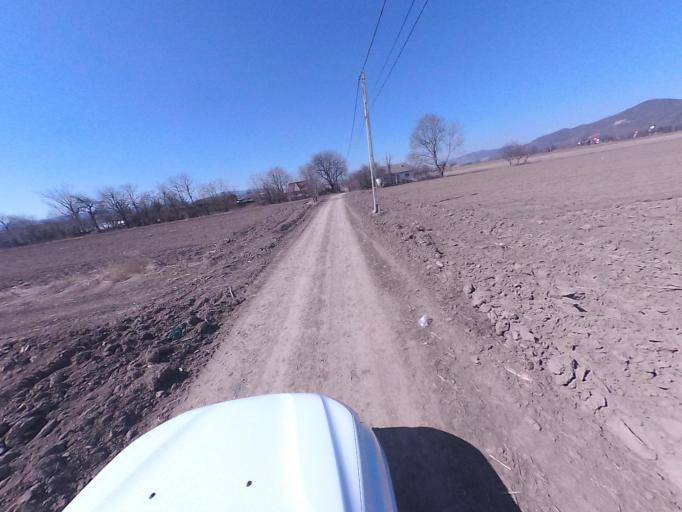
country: RO
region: Neamt
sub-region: Oras Targu Neamt
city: Humulesti
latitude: 47.1915
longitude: 26.3563
